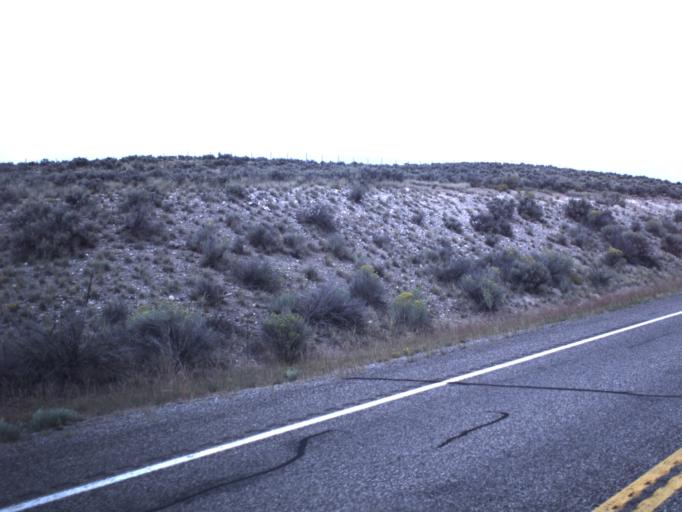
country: US
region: Utah
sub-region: Garfield County
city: Panguitch
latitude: 38.0087
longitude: -112.3771
